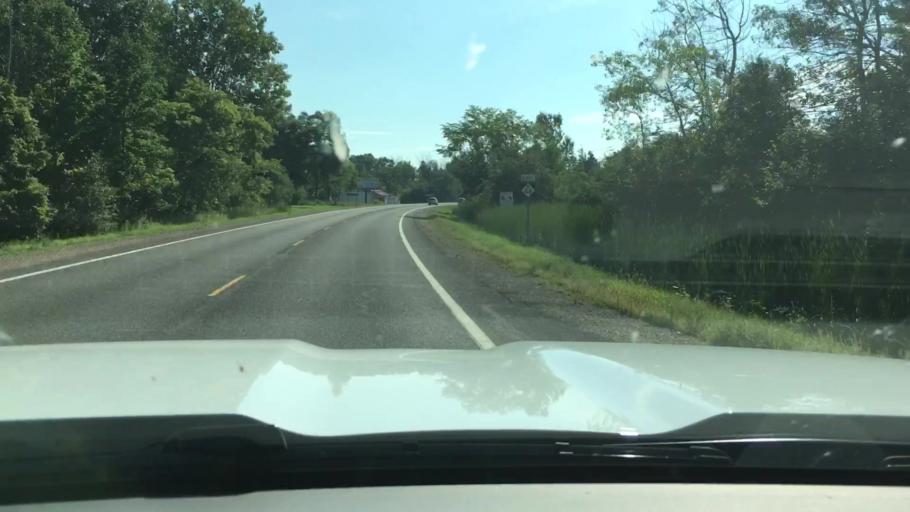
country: US
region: Michigan
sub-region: Montcalm County
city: Edmore
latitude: 43.4080
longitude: -84.9849
